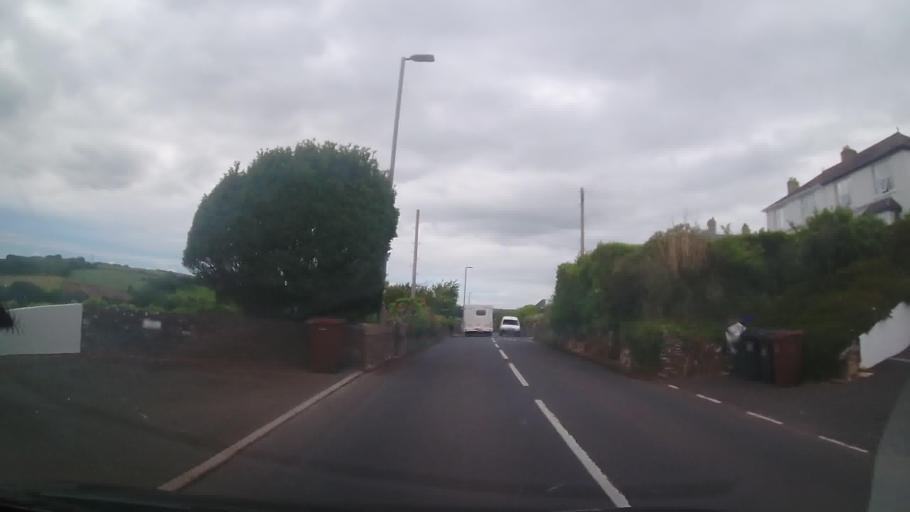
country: GB
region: England
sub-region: Devon
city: Kingsbridge
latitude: 50.2729
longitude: -3.7684
